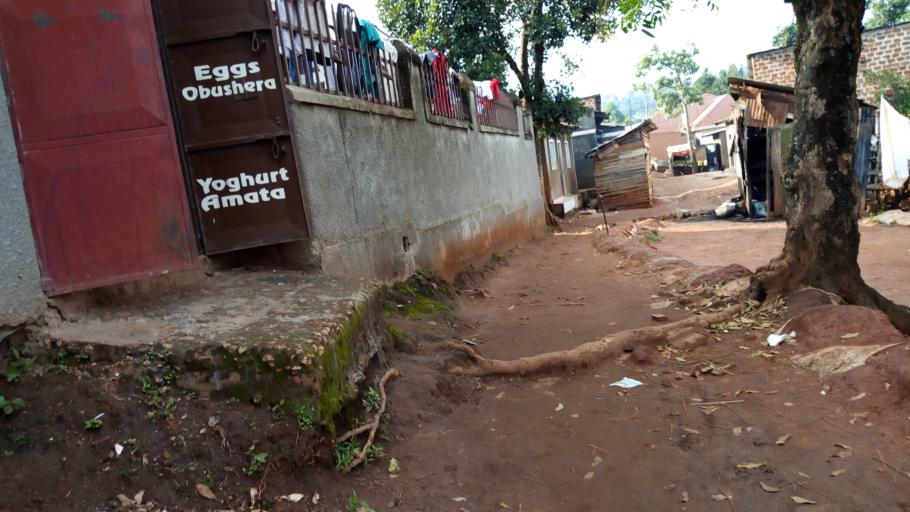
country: UG
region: Central Region
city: Kampala Central Division
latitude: 0.3727
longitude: 32.5533
